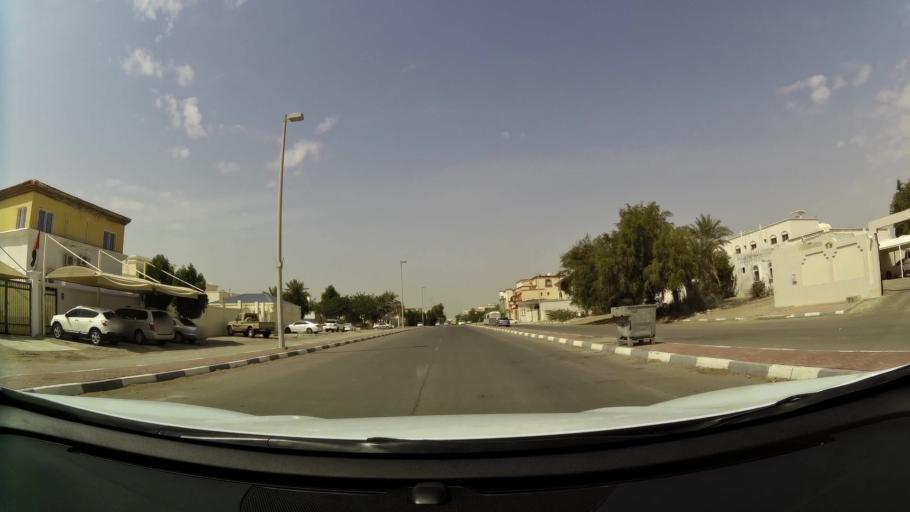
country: AE
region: Abu Dhabi
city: Abu Dhabi
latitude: 24.2982
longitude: 54.6435
